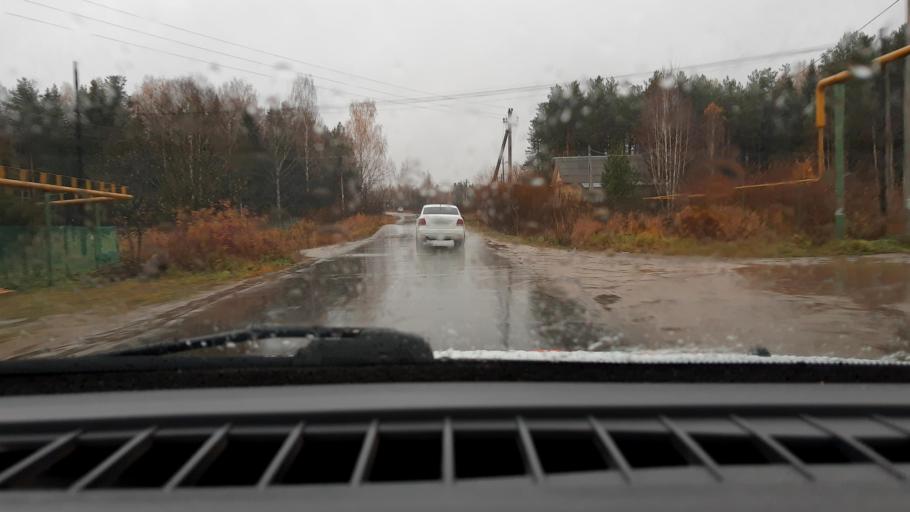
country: RU
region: Nizjnij Novgorod
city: Linda
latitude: 56.6802
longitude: 44.1959
